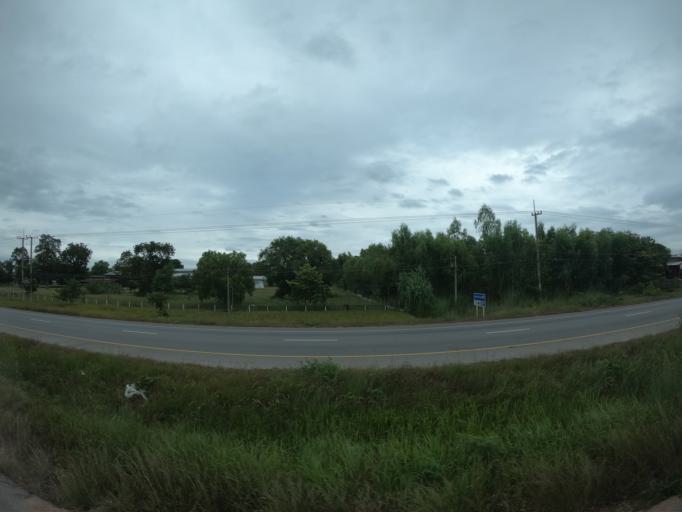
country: TH
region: Roi Et
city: Changhan
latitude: 16.0829
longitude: 103.5698
